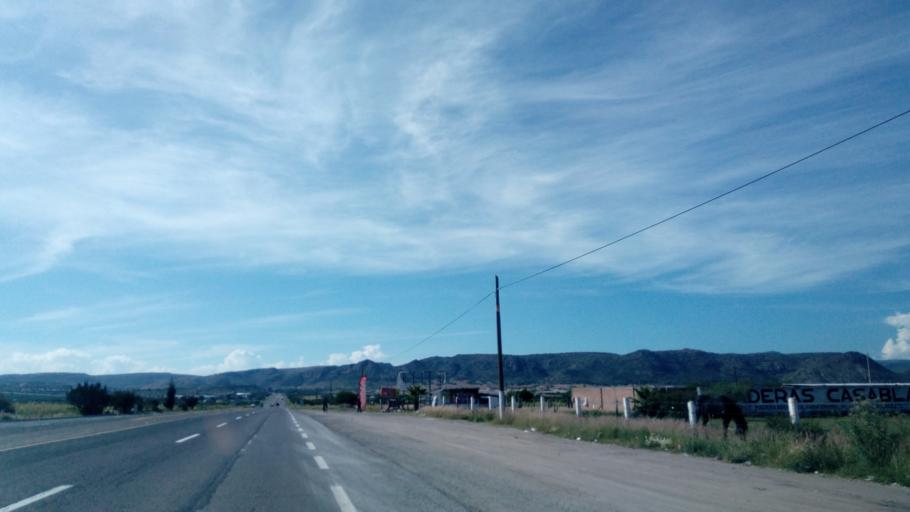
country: MX
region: Durango
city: Victoria de Durango
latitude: 24.1455
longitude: -104.7098
